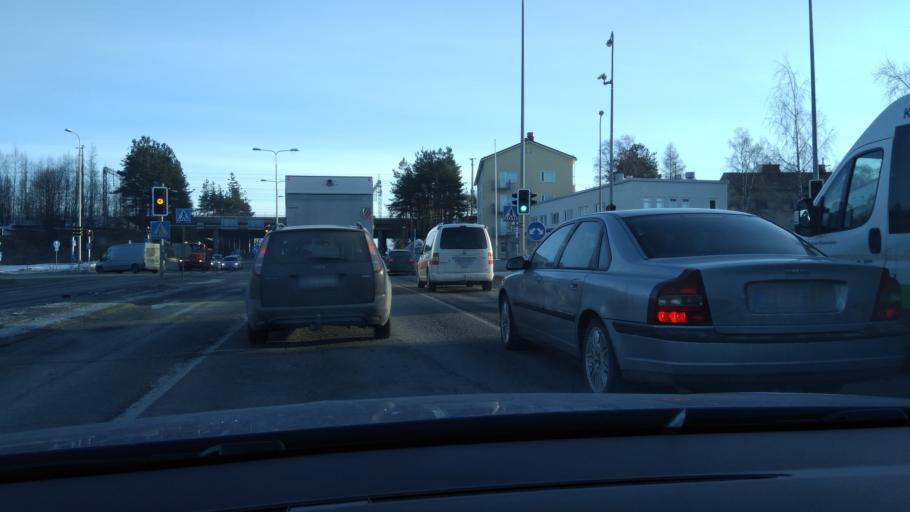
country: FI
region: Pirkanmaa
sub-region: Tampere
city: Pirkkala
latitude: 61.5078
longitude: 23.6877
